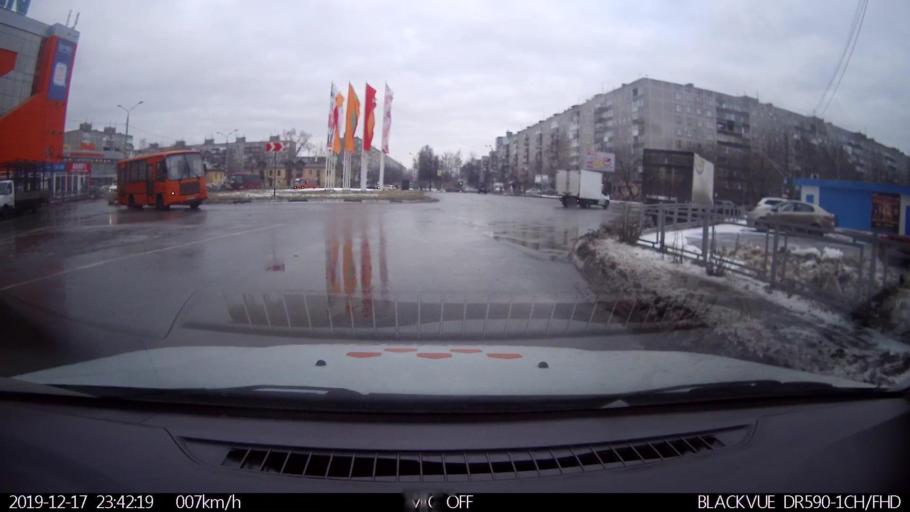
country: RU
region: Nizjnij Novgorod
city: Gorbatovka
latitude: 56.3639
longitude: 43.8156
